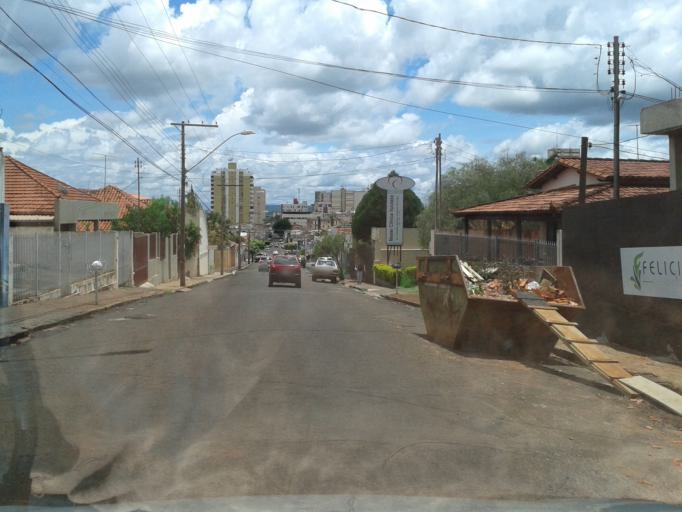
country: BR
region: Minas Gerais
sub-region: Ituiutaba
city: Ituiutaba
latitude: -18.9787
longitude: -49.4637
